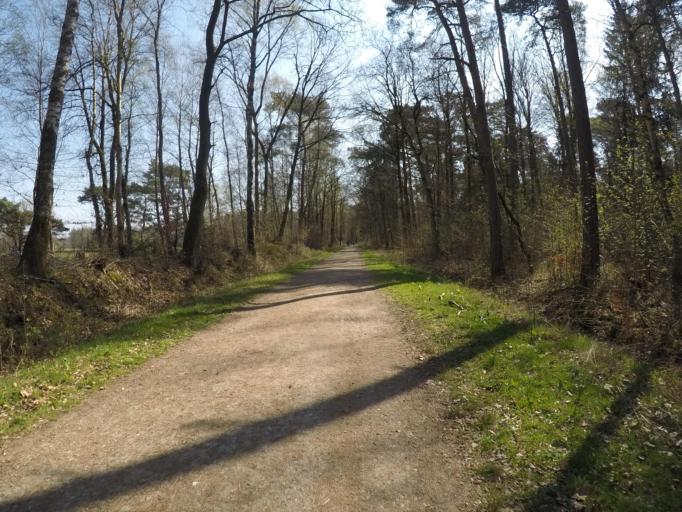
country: DE
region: Schleswig-Holstein
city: Rellingen
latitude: 53.6144
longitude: 9.7765
